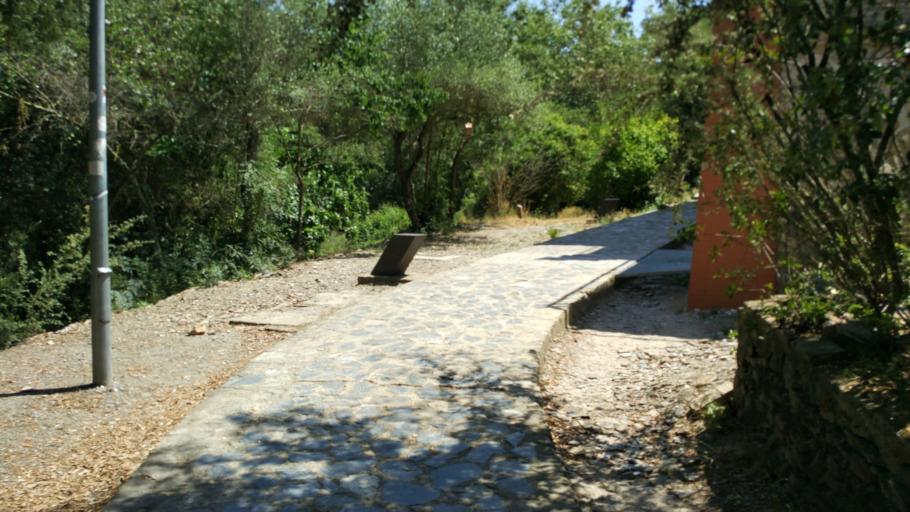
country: ES
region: Catalonia
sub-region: Provincia de Barcelona
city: Sant Just Desvern
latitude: 41.4199
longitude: 2.0995
